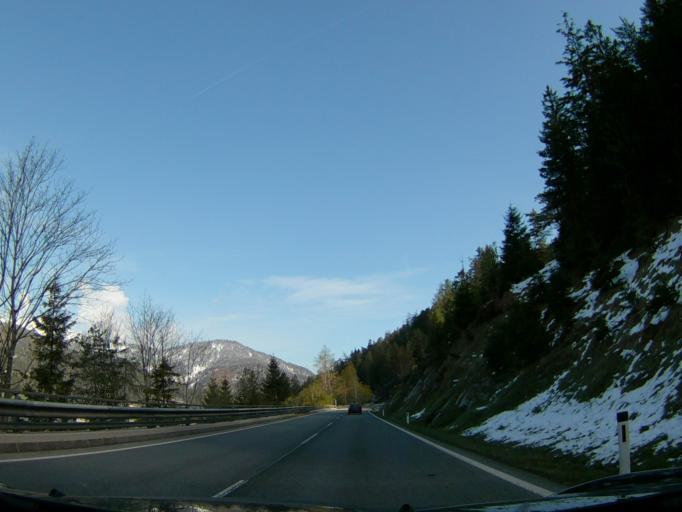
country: AT
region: Tyrol
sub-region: Politischer Bezirk Schwaz
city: Achenkirch
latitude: 47.4966
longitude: 11.7117
